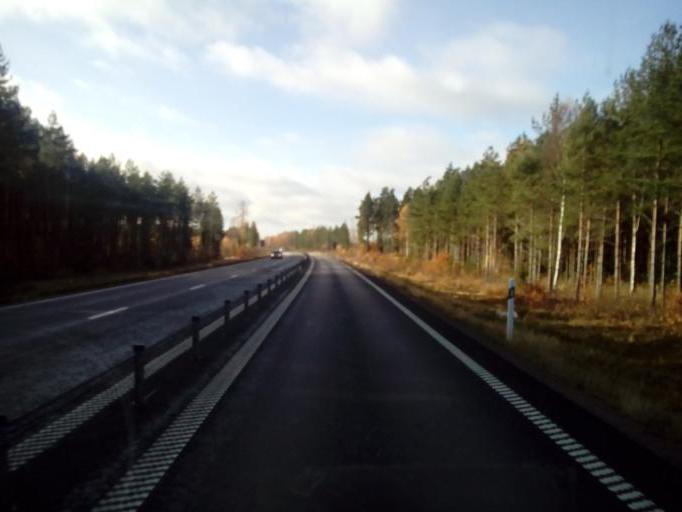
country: SE
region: Kalmar
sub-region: Vimmerby Kommun
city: Vimmerby
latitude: 57.6786
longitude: 15.9464
